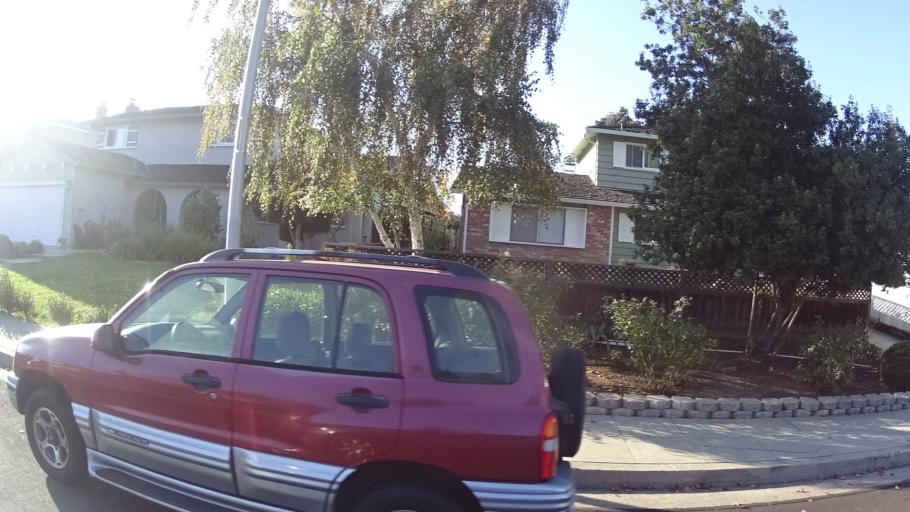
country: US
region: California
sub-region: Santa Clara County
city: Santa Clara
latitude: 37.3431
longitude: -121.9845
